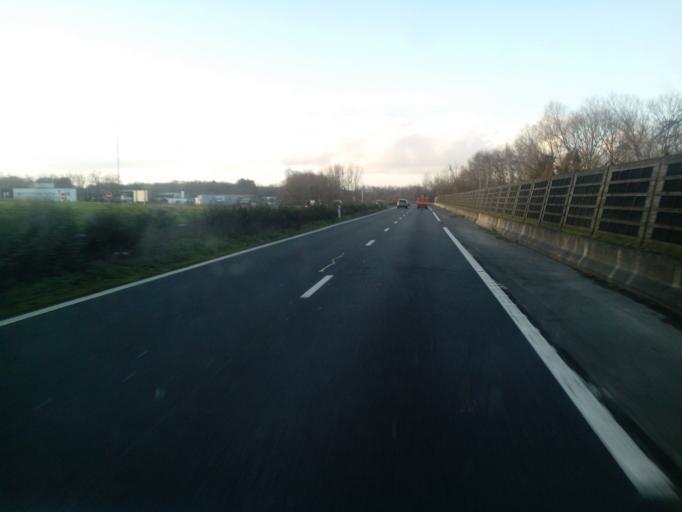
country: FR
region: Pays de la Loire
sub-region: Departement de la Loire-Atlantique
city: Haute-Goulaine
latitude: 47.1812
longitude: -1.4128
